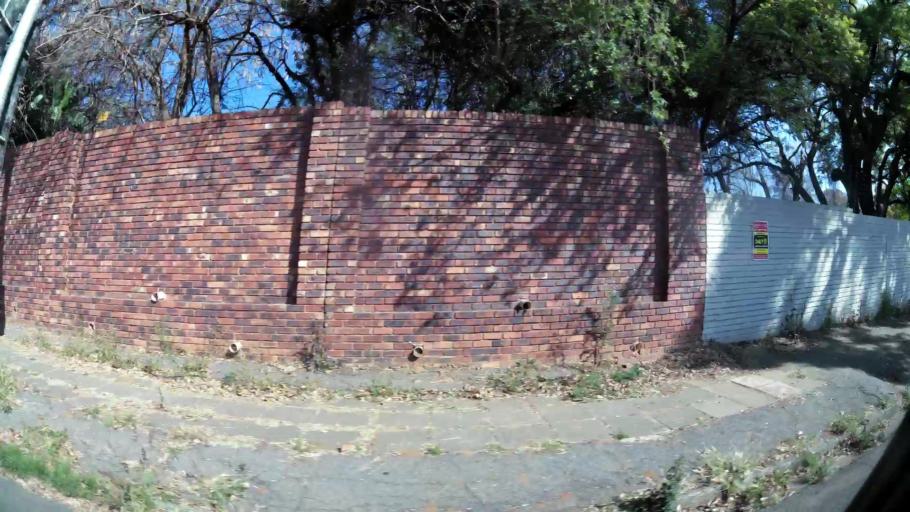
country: ZA
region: Gauteng
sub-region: City of Johannesburg Metropolitan Municipality
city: Johannesburg
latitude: -26.1609
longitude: 28.0291
